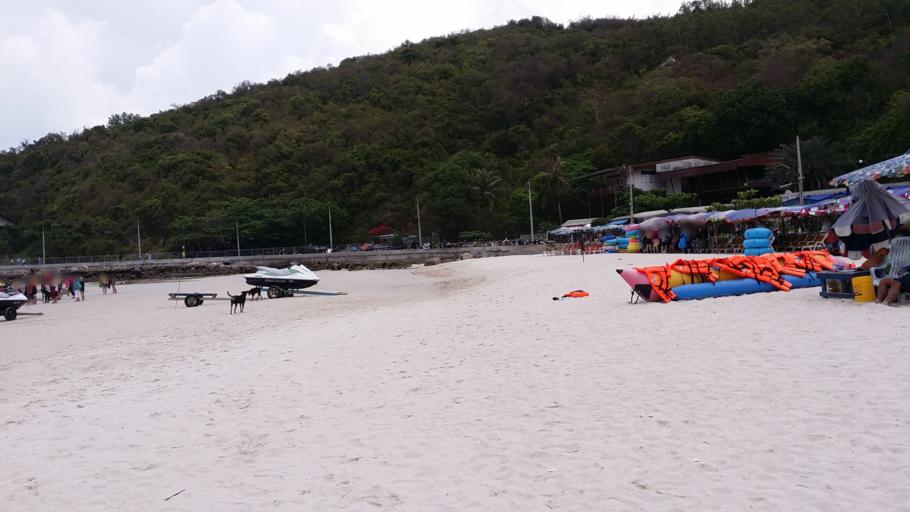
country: TH
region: Chon Buri
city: Ban Ko Lan
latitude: 12.9258
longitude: 100.7802
